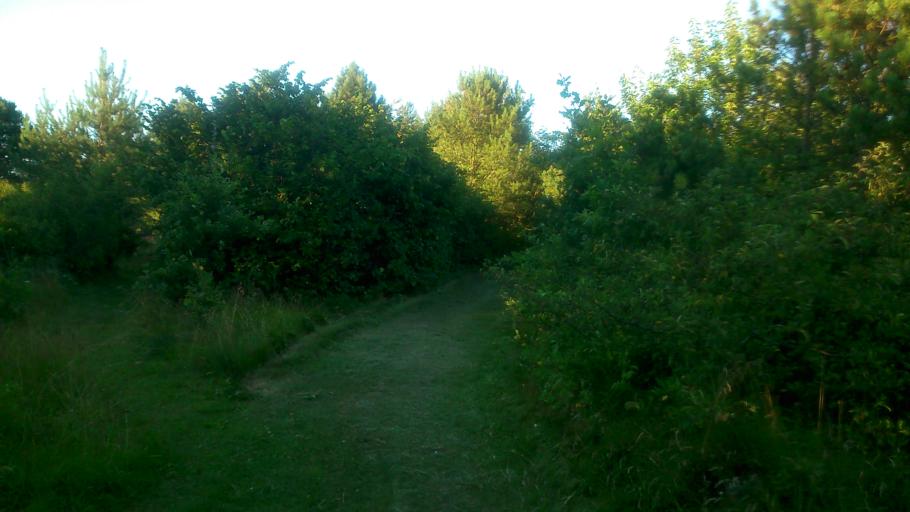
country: DK
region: Central Jutland
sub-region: Ringkobing-Skjern Kommune
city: Skjern
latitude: 55.9395
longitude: 8.5131
